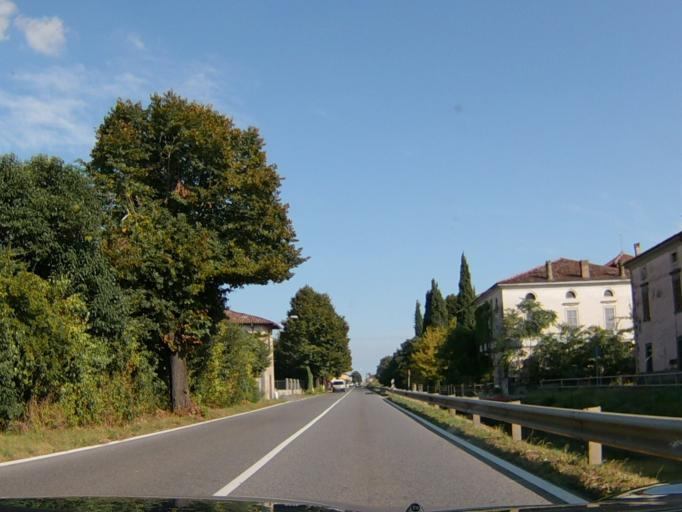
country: IT
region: Lombardy
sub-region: Provincia di Brescia
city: Cologne
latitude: 45.5799
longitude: 9.9320
